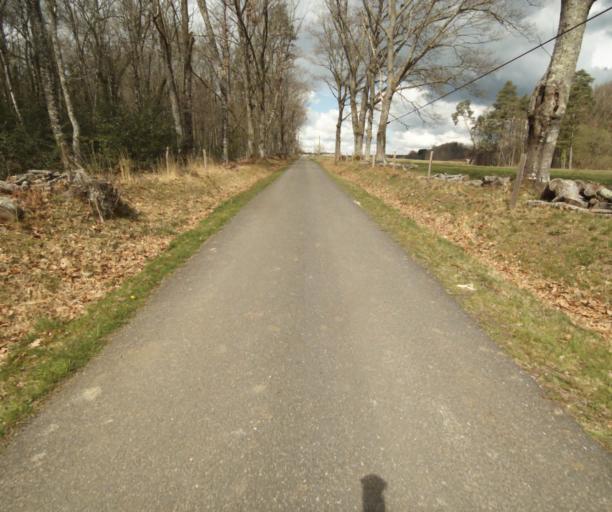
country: FR
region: Limousin
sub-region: Departement de la Correze
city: Correze
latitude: 45.2538
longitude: 1.9065
